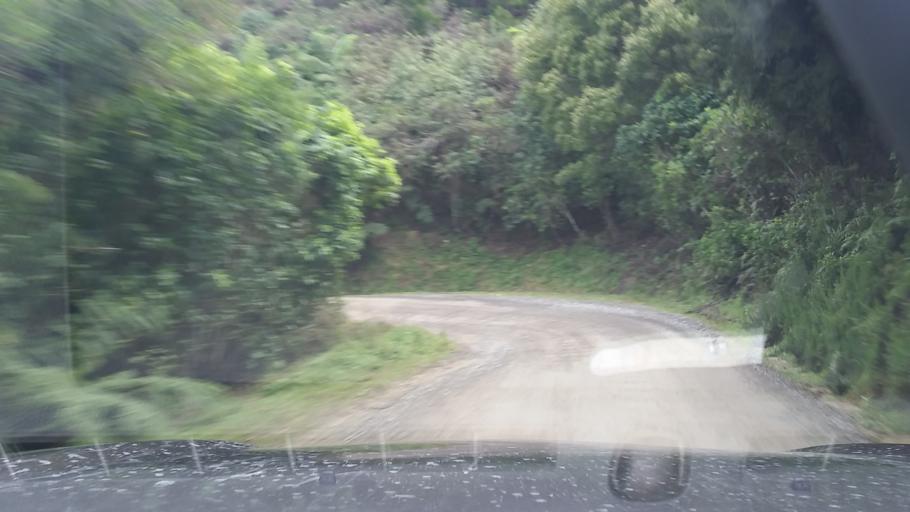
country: NZ
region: Marlborough
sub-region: Marlborough District
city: Picton
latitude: -41.1773
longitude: 174.0745
